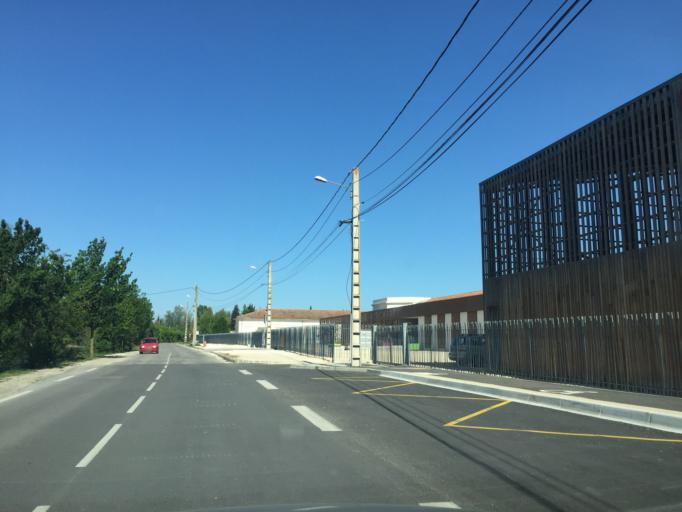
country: FR
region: Provence-Alpes-Cote d'Azur
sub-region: Departement du Vaucluse
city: L'Isle-sur-la-Sorgue
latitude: 43.9251
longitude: 5.0361
